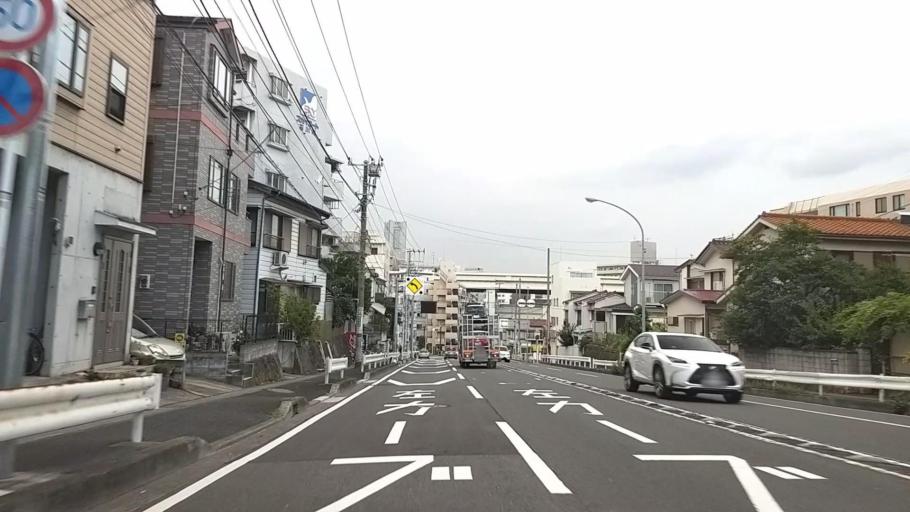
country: JP
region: Kanagawa
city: Yokohama
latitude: 35.4353
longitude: 139.6382
